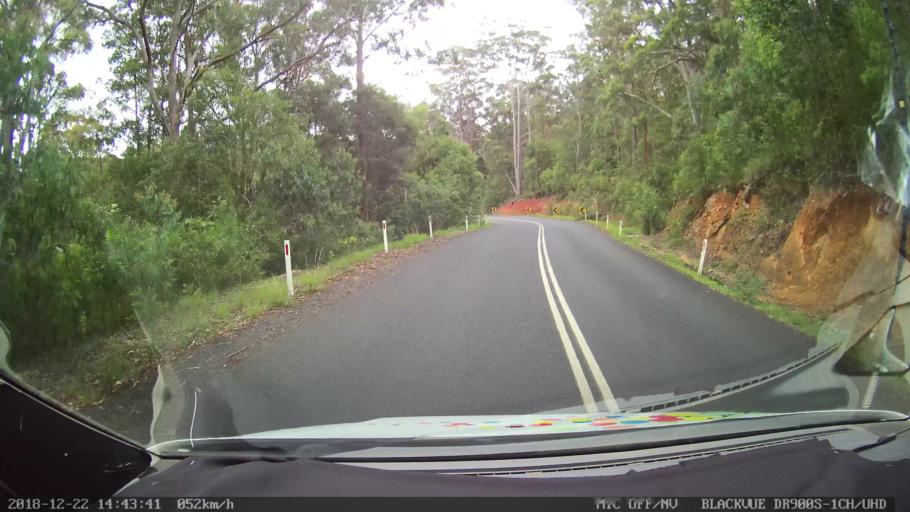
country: AU
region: New South Wales
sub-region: Bellingen
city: Dorrigo
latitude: -30.1651
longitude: 152.5823
